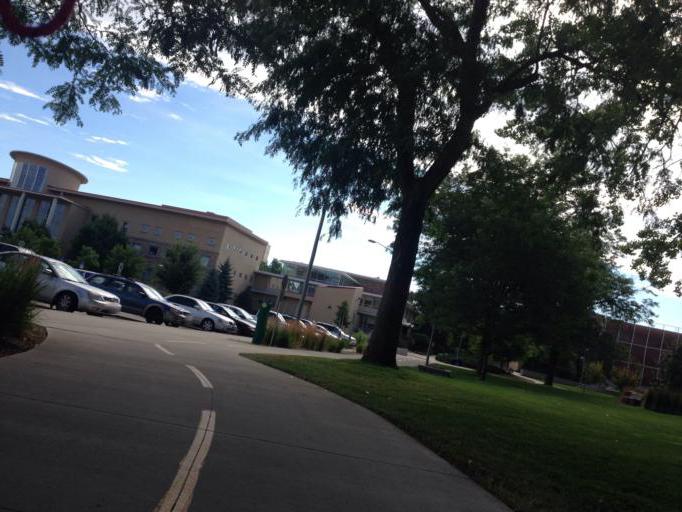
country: US
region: Colorado
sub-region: Larimer County
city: Fort Collins
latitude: 40.5726
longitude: -105.0860
